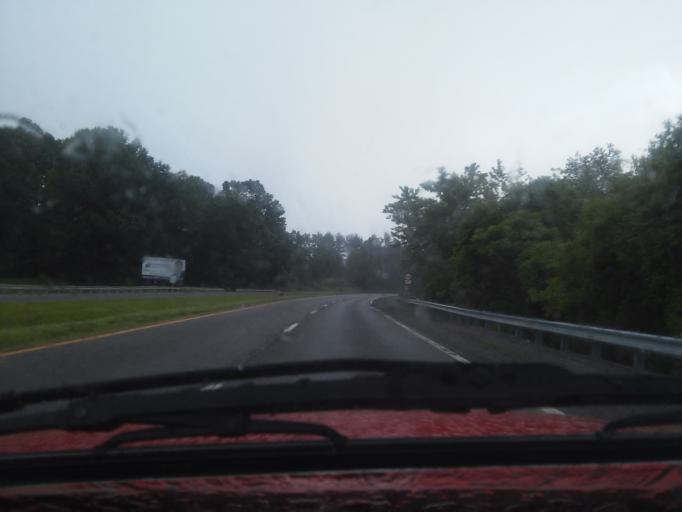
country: US
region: Virginia
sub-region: Montgomery County
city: Prices Fork
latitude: 37.2986
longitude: -80.5033
